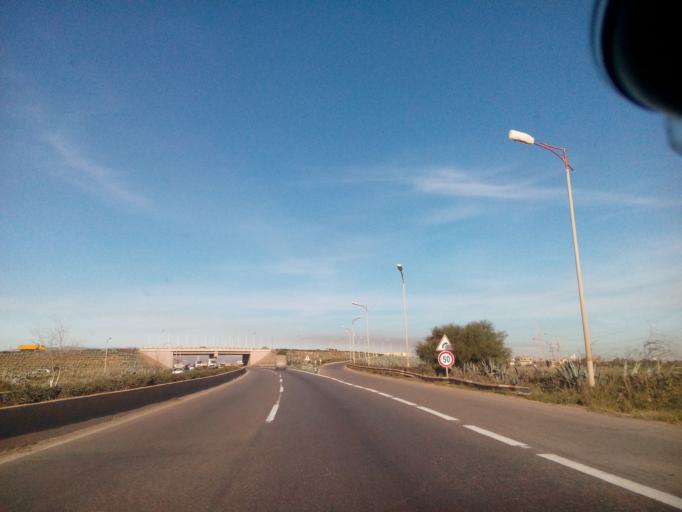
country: DZ
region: Oran
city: Ain el Bya
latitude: 35.7984
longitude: -0.2922
